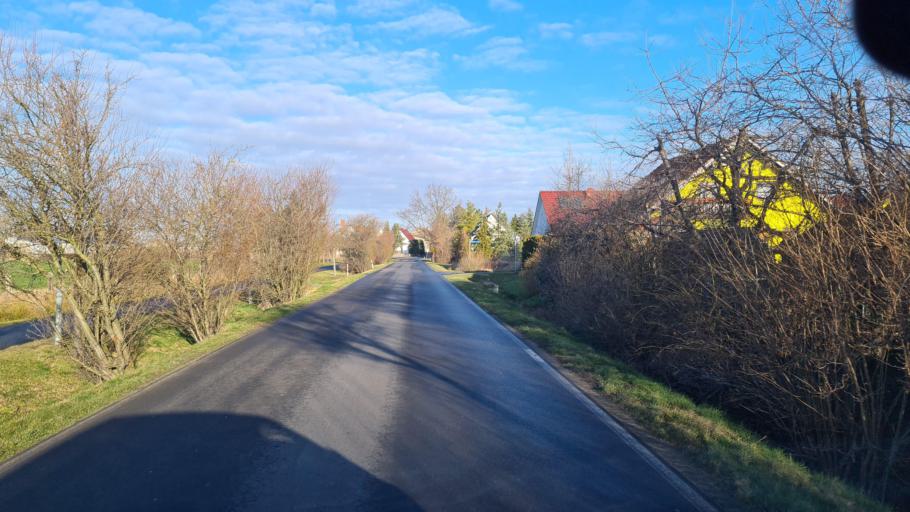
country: DE
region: Brandenburg
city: Herzberg
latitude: 51.6965
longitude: 13.2204
